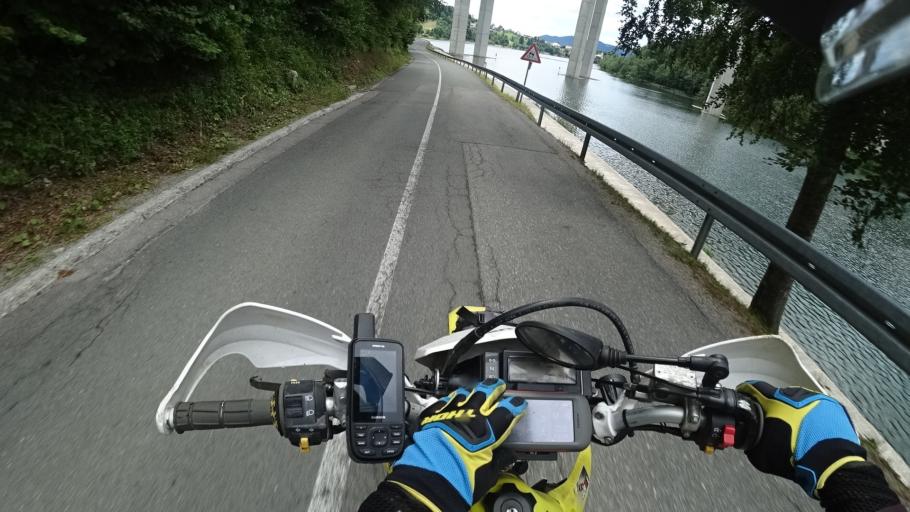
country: HR
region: Primorsko-Goranska
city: Hreljin
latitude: 45.3182
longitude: 14.7103
